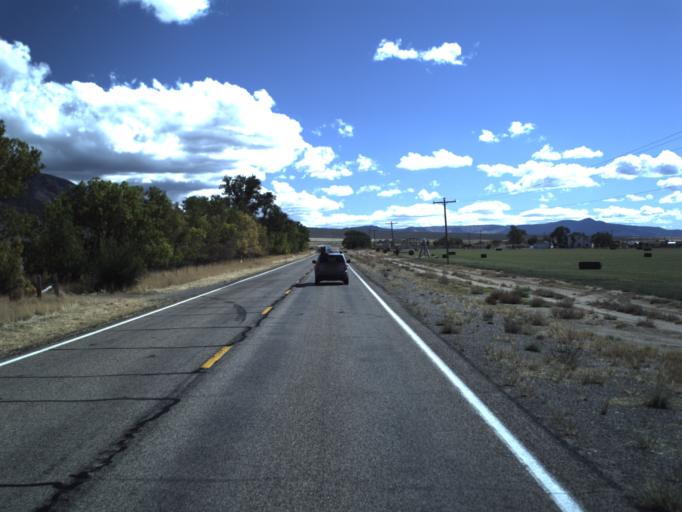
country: US
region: Utah
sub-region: Beaver County
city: Milford
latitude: 38.3428
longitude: -112.9791
